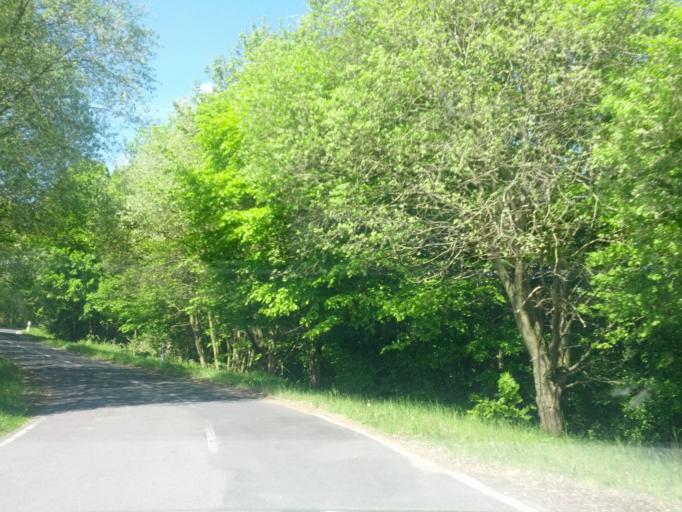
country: DE
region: Thuringia
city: Treffurt
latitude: 51.1112
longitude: 10.2032
